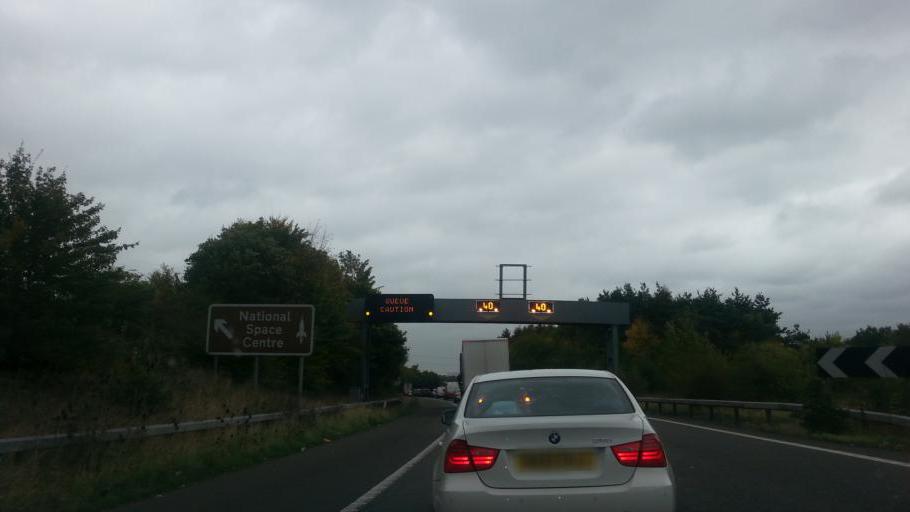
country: GB
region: England
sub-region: Leicestershire
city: Enderby
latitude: 52.5978
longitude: -1.2125
